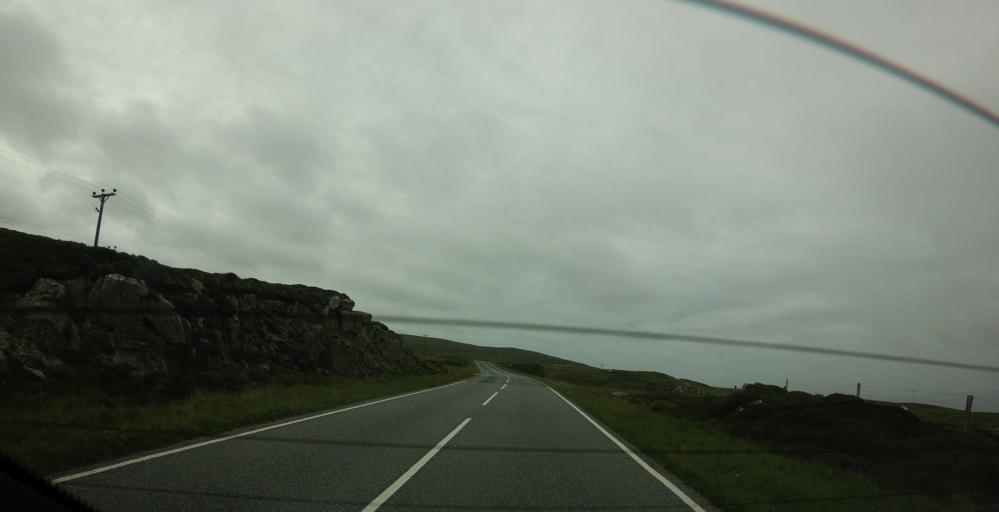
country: GB
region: Scotland
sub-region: Eilean Siar
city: Isle of South Uist
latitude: 57.2435
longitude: -7.3837
